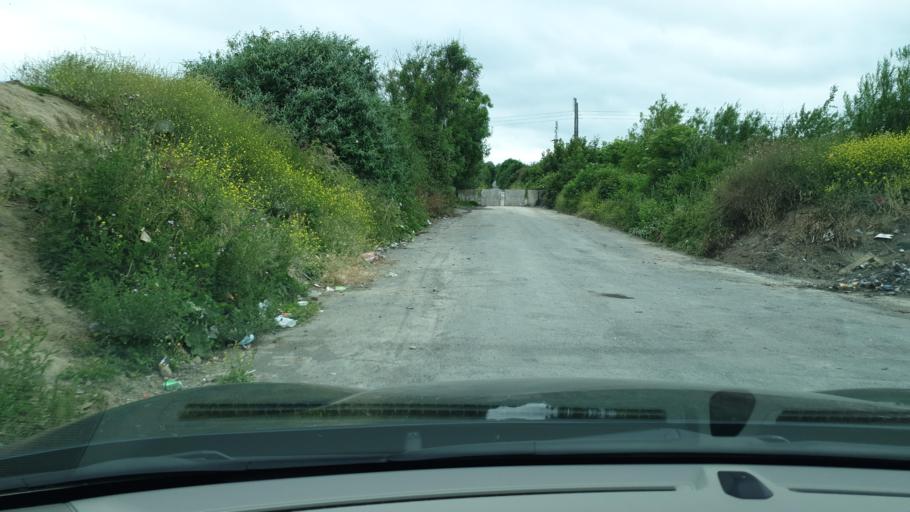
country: IE
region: Leinster
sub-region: Dublin City
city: Finglas
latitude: 53.3861
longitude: -6.3255
